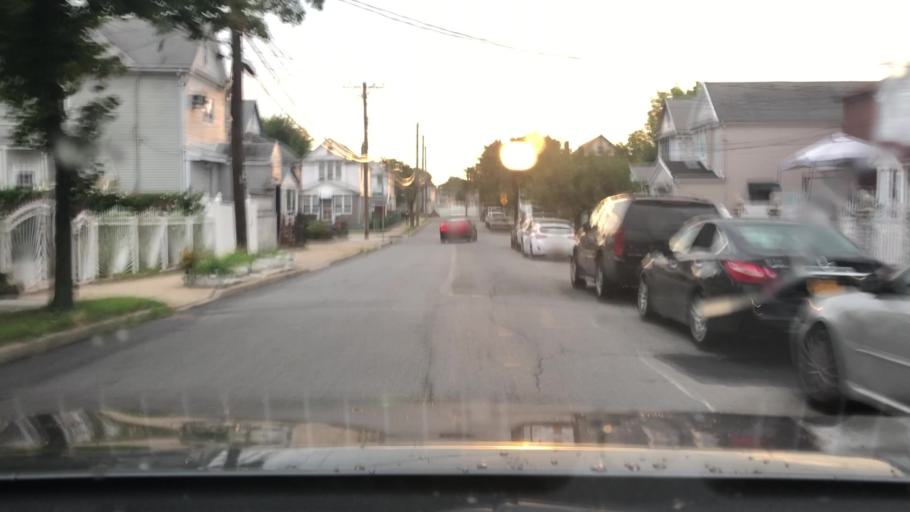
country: US
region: New York
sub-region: Queens County
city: Jamaica
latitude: 40.6692
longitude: -73.8061
